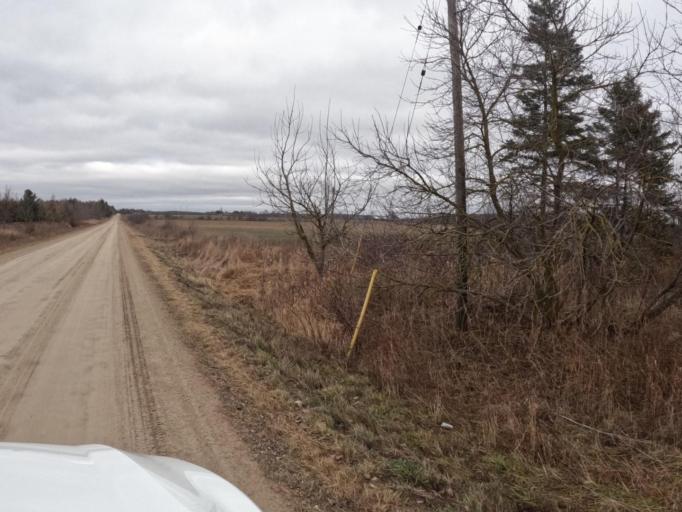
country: CA
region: Ontario
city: Shelburne
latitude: 43.9416
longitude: -80.3948
